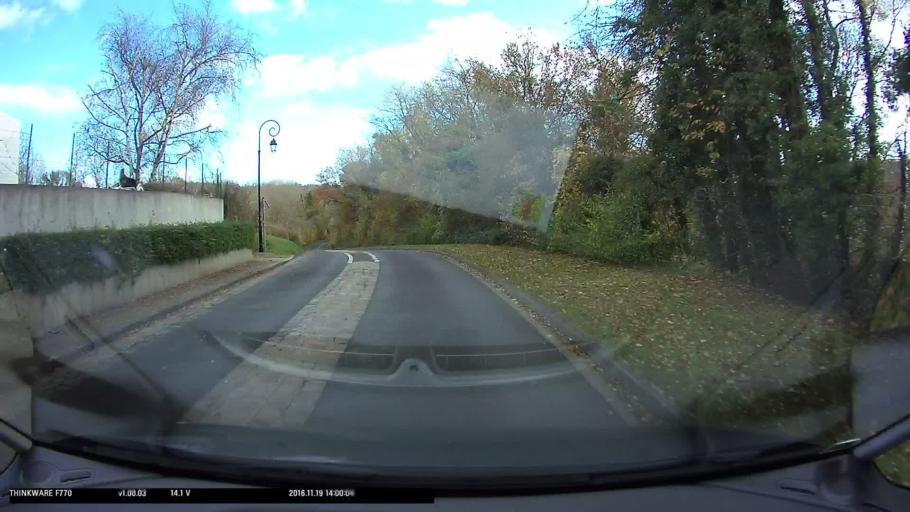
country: FR
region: Ile-de-France
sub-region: Departement du Val-d'Oise
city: Ableiges
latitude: 49.0887
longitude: 1.9892
